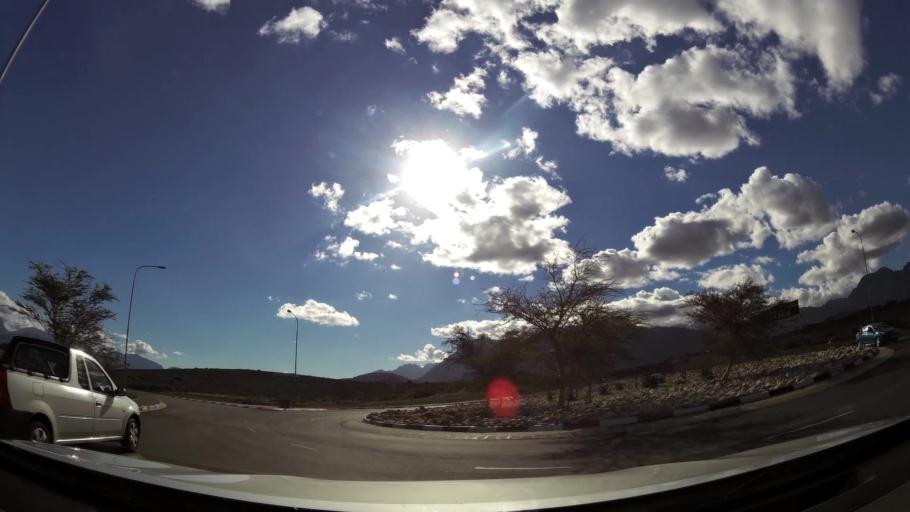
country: ZA
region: Western Cape
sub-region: Cape Winelands District Municipality
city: Worcester
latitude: -33.6348
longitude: 19.4278
